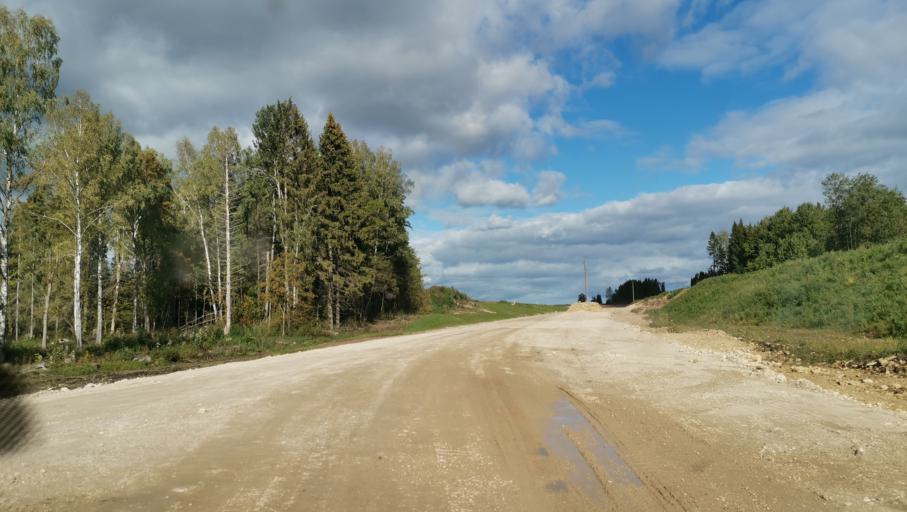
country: EE
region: Harju
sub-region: Nissi vald
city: Riisipere
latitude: 59.1310
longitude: 24.4801
